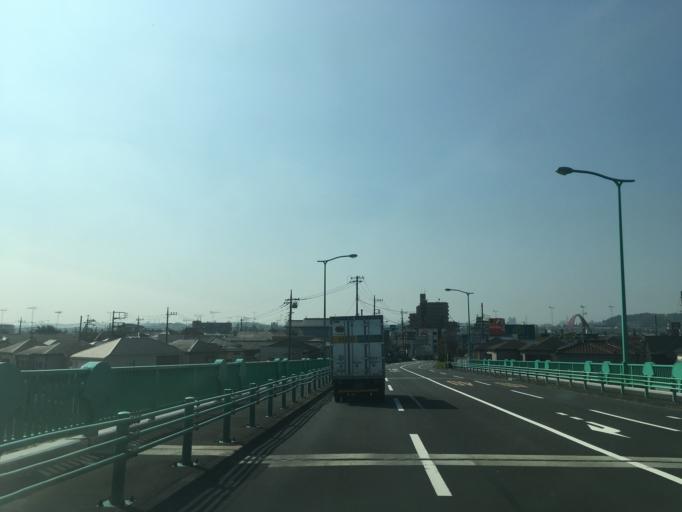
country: JP
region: Tokyo
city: Hino
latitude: 35.7003
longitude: 139.3773
